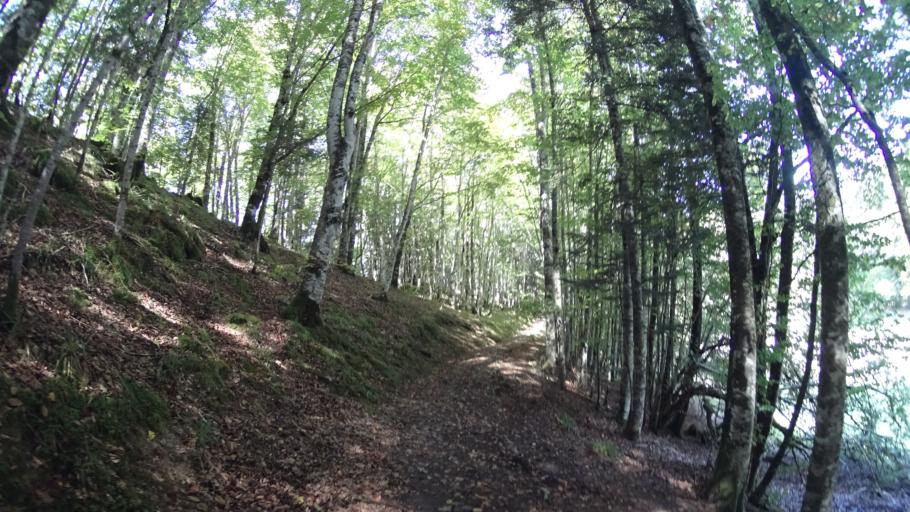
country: ES
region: Navarre
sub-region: Provincia de Navarra
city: Orbara
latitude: 42.9864
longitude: -1.1382
